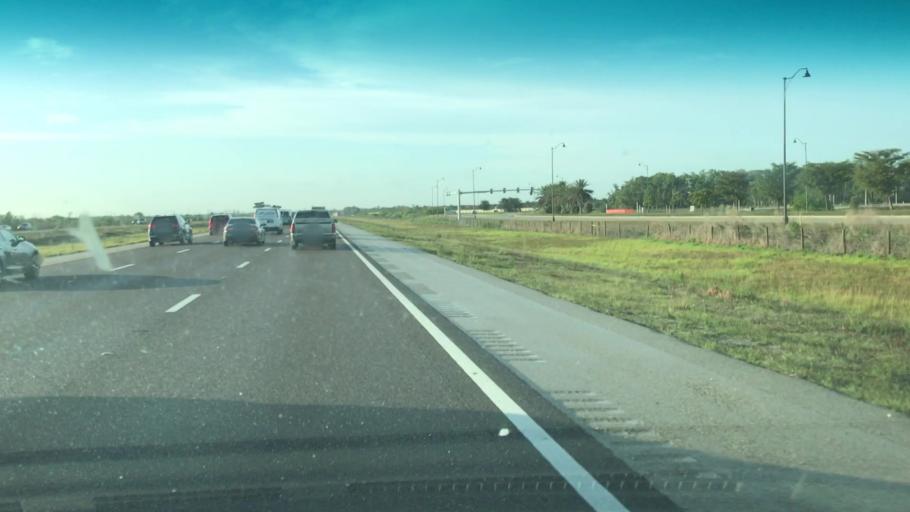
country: US
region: Florida
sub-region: Lee County
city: Bonita Springs
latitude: 26.3690
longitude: -81.7694
